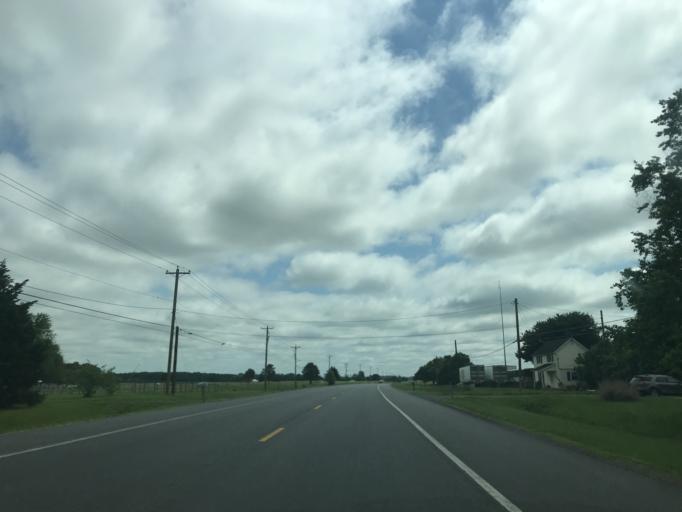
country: US
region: Maryland
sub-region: Caroline County
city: Ridgely
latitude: 38.9258
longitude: -75.9275
